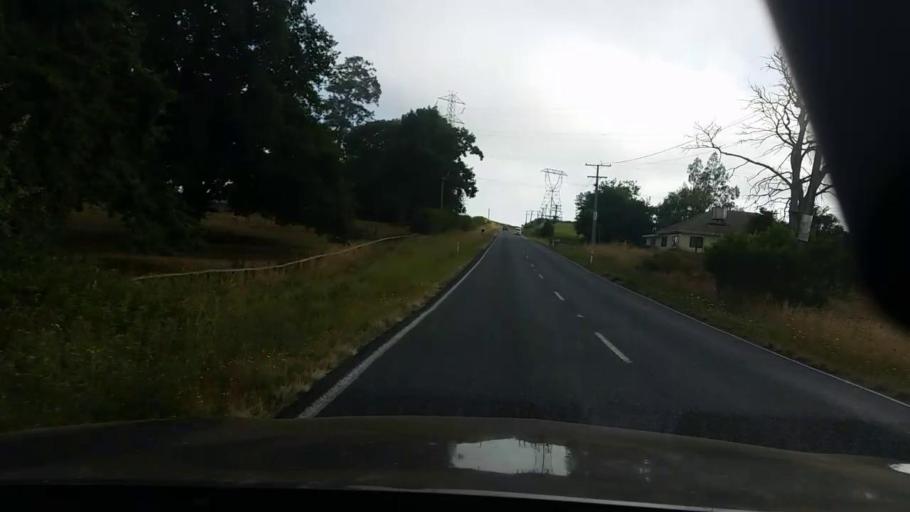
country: NZ
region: Waikato
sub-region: Hamilton City
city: Hamilton
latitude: -37.6185
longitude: 175.3387
